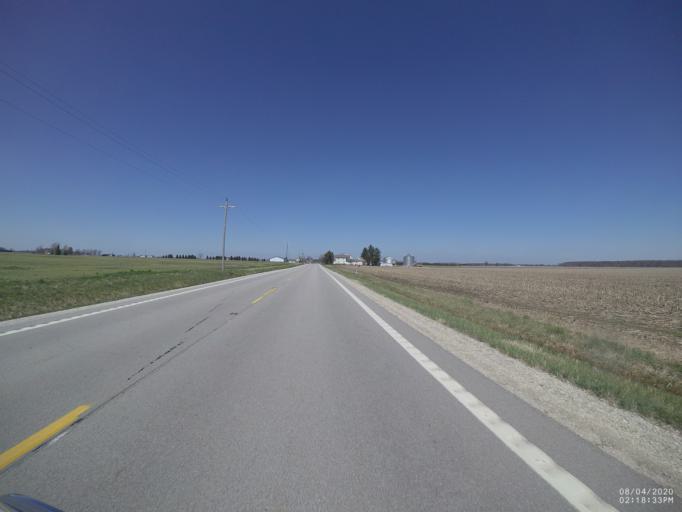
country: US
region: Ohio
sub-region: Sandusky County
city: Stony Prairie
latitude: 41.2869
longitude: -83.2354
